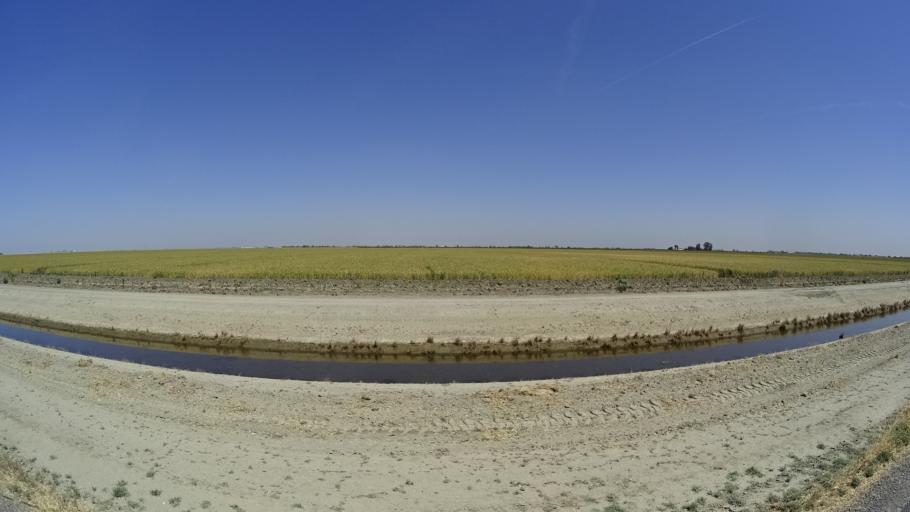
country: US
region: California
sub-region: Kings County
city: Corcoran
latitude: 36.0217
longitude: -119.5476
